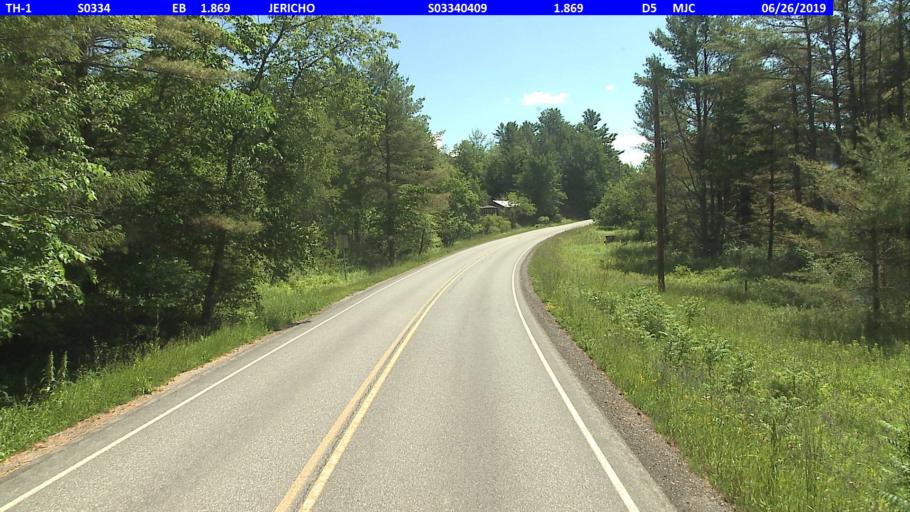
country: US
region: Vermont
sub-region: Chittenden County
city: Jericho
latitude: 44.4629
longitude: -72.9852
